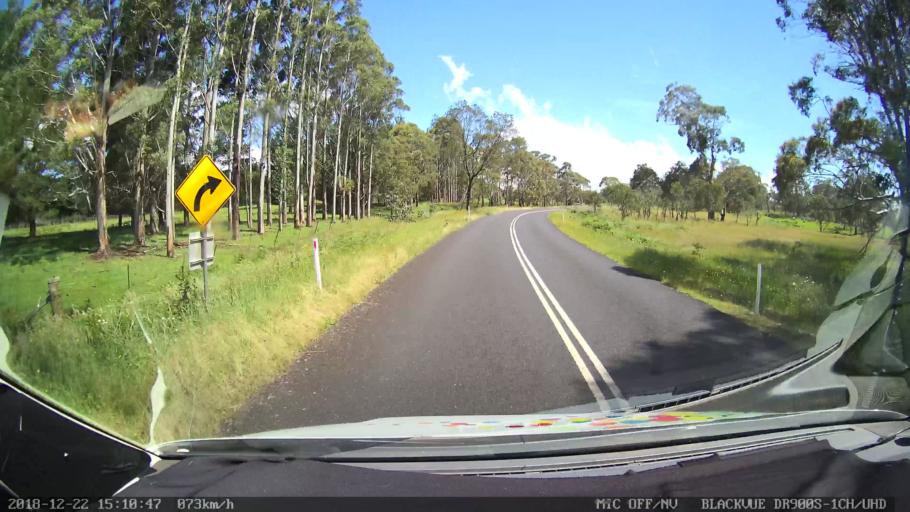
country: AU
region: New South Wales
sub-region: Bellingen
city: Dorrigo
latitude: -30.3385
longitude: 152.4065
